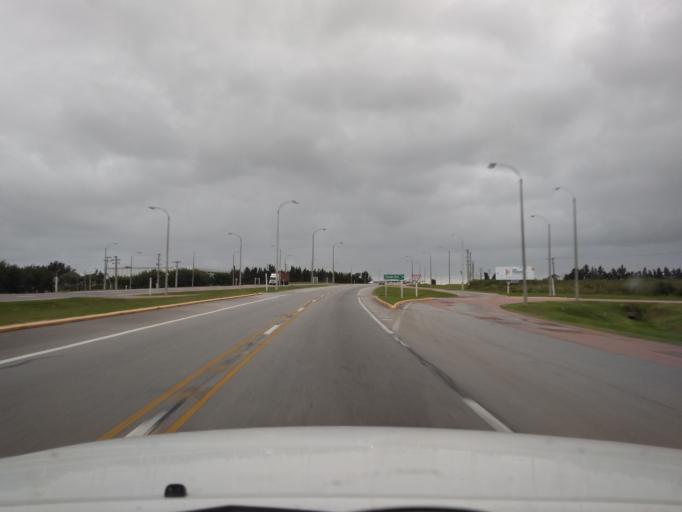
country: UY
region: Canelones
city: Progreso
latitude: -34.6948
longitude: -56.2384
